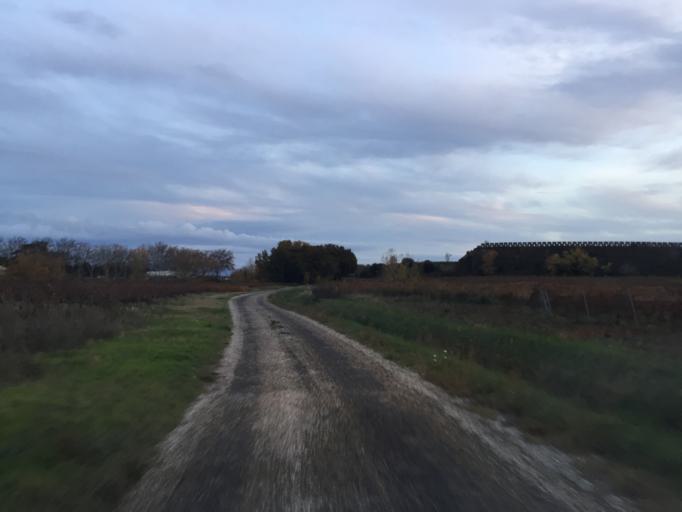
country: FR
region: Provence-Alpes-Cote d'Azur
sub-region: Departement du Vaucluse
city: Courthezon
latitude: 44.0699
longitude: 4.8813
